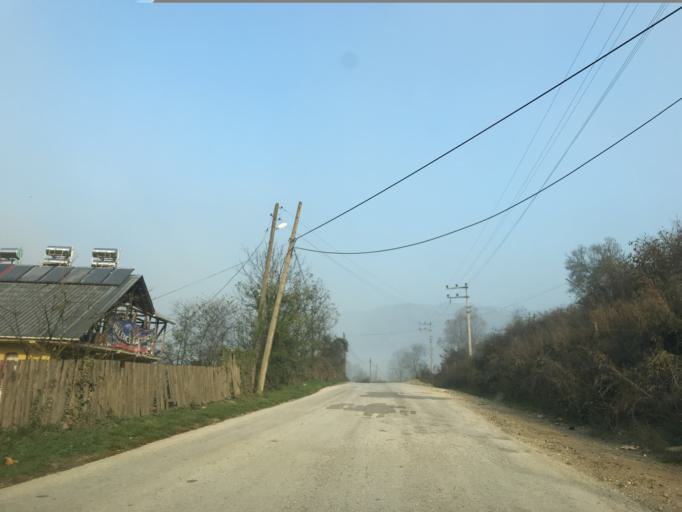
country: TR
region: Duzce
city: Cumayeri
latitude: 40.9049
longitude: 30.9517
